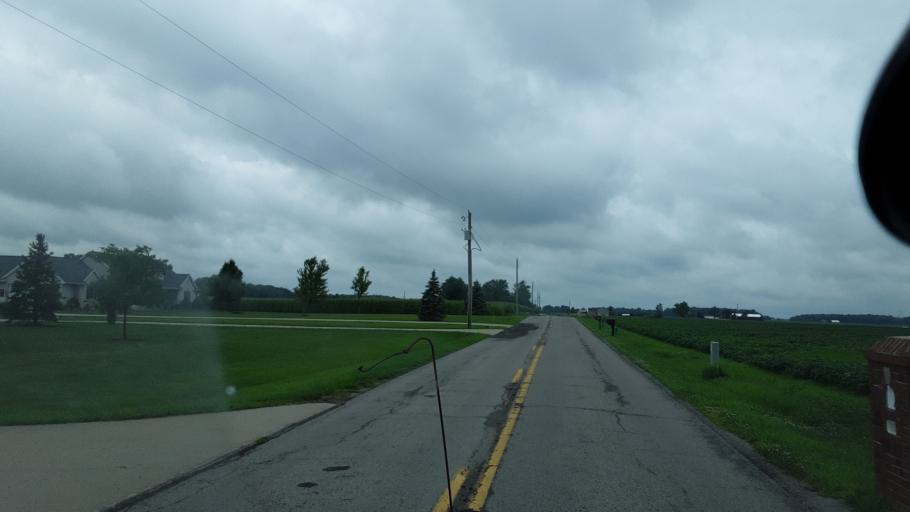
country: US
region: Indiana
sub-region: Wells County
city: Ossian
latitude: 40.9322
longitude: -85.1059
